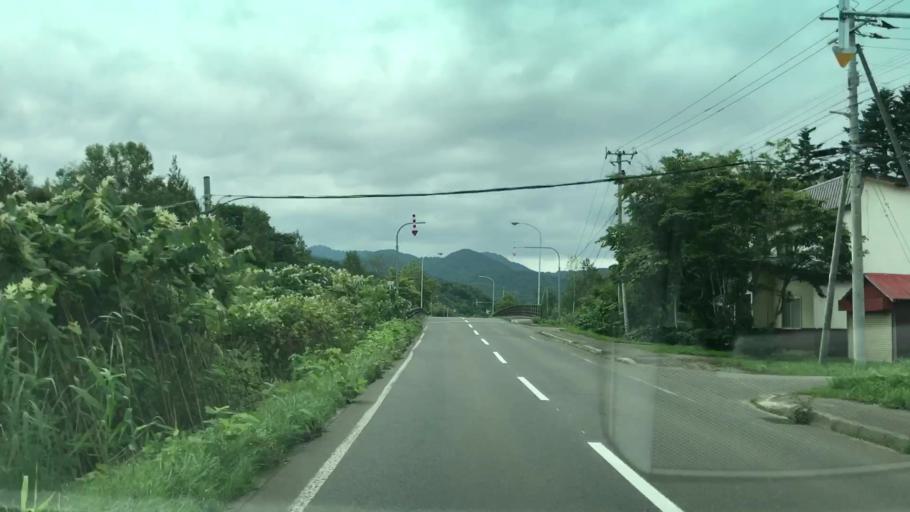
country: JP
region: Hokkaido
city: Yoichi
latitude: 43.0603
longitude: 140.8214
